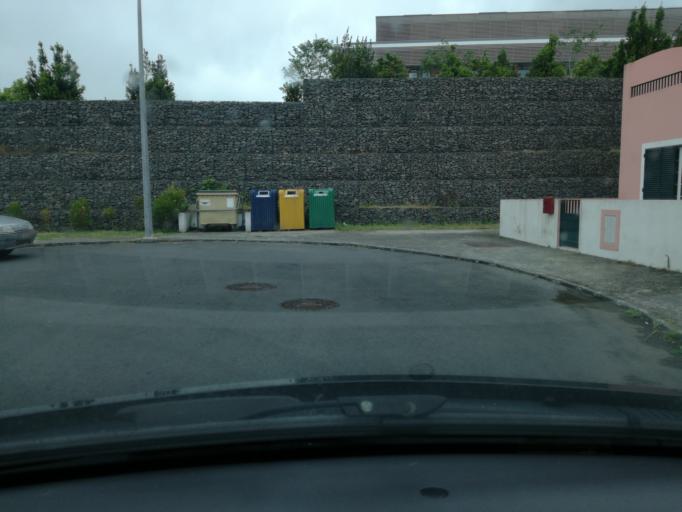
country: PT
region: Azores
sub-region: Angra do Heroismo
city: Angra do Heroismo
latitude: 38.6708
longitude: -27.2145
